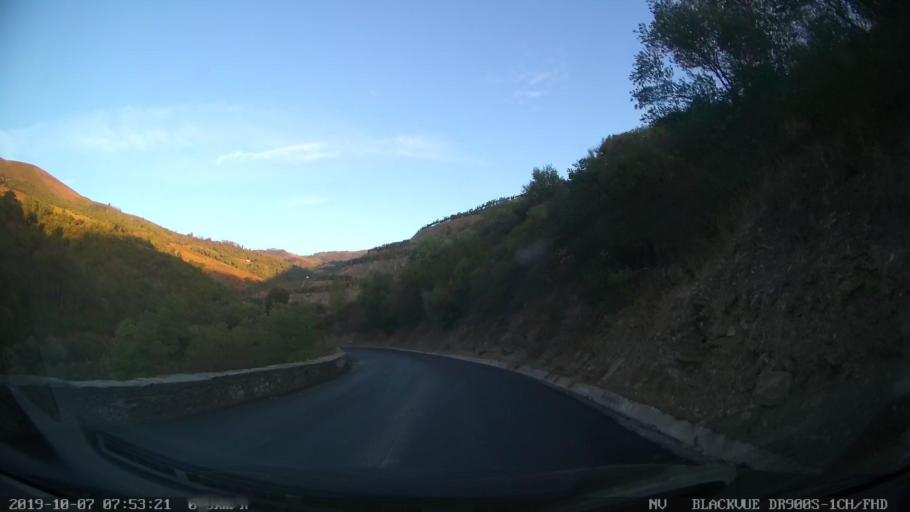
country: PT
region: Vila Real
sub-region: Sabrosa
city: Vilela
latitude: 41.2038
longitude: -7.5639
